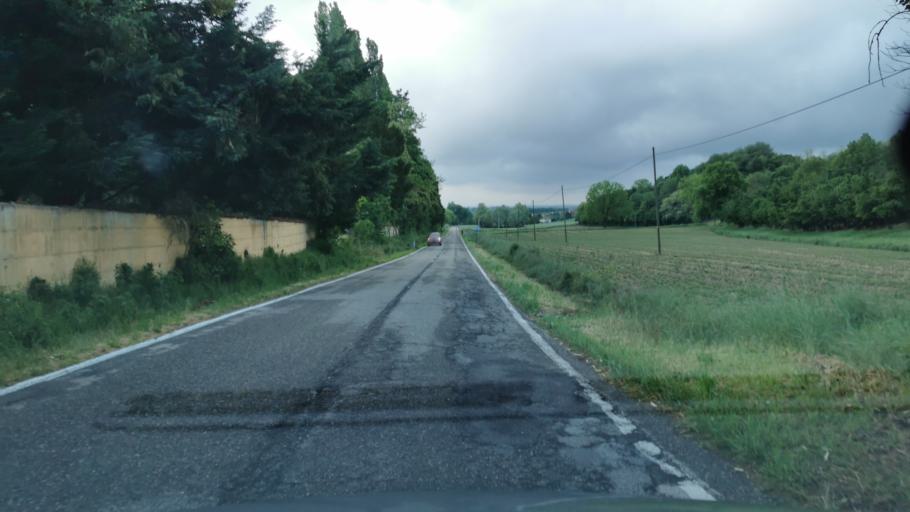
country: IT
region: Piedmont
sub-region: Provincia di Torino
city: Pino Torinese
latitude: 45.0105
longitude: 7.7814
